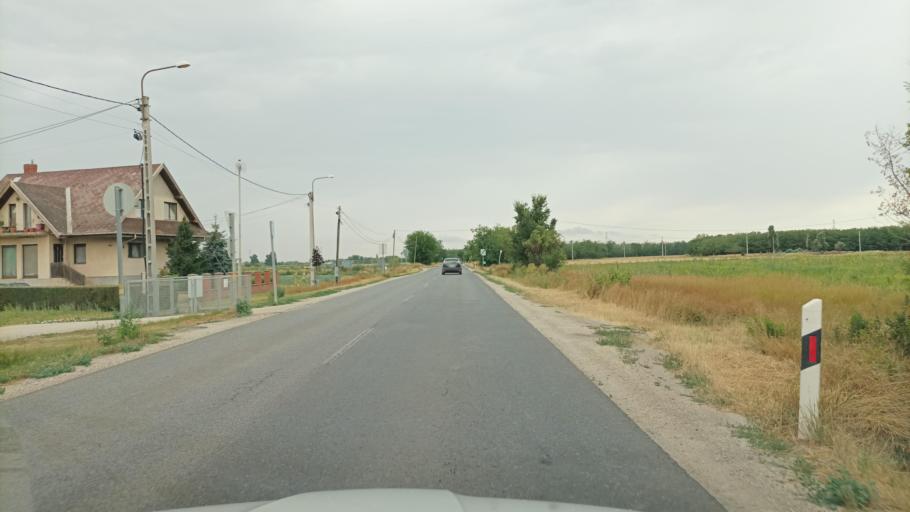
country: HU
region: Pest
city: Bugyi
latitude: 47.2383
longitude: 19.1356
